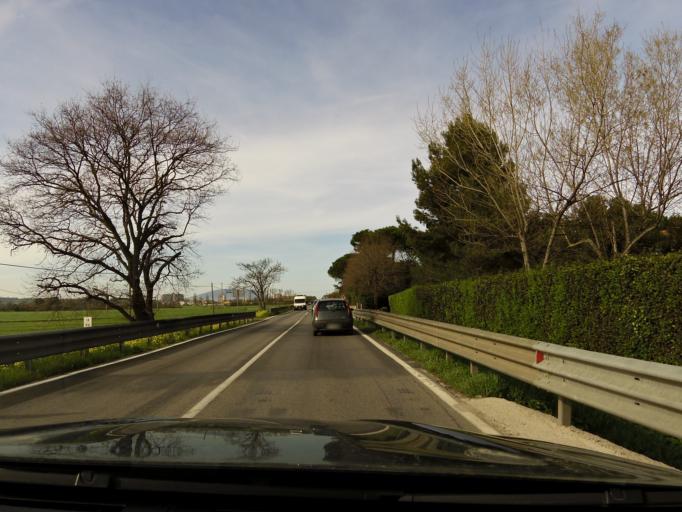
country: IT
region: The Marches
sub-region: Provincia di Macerata
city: Porto Recanati
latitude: 43.3952
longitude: 13.6795
